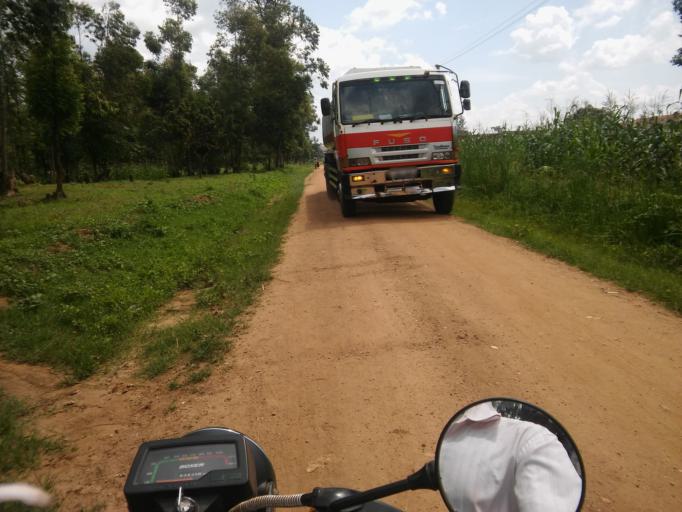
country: UG
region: Eastern Region
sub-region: Mbale District
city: Mbale
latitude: 1.0748
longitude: 34.1576
